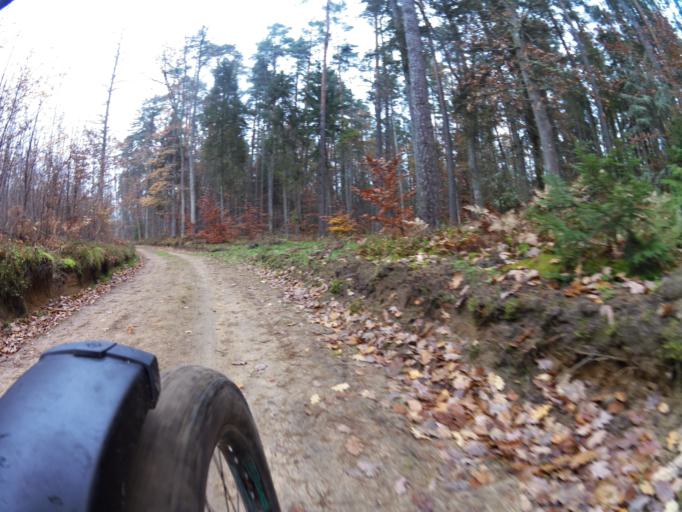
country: PL
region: Pomeranian Voivodeship
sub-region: Powiat wejherowski
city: Orle
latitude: 54.6962
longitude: 18.1568
